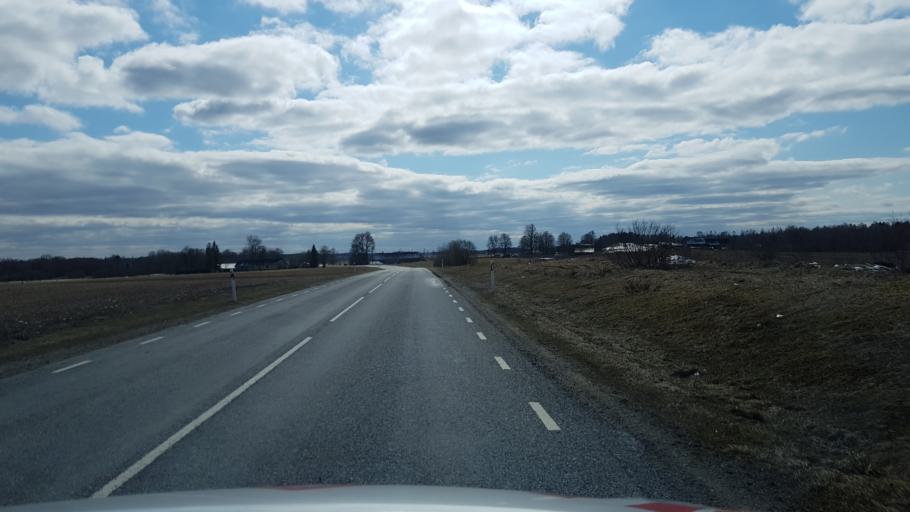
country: EE
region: Laeaene-Virumaa
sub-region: Tapa vald
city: Tapa
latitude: 59.3311
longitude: 26.0001
